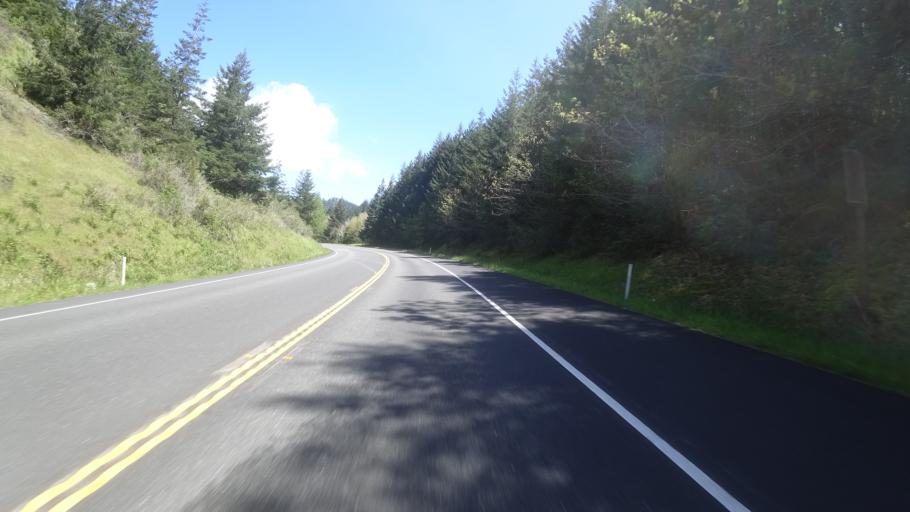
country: US
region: California
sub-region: Humboldt County
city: Blue Lake
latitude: 40.9003
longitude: -123.9186
